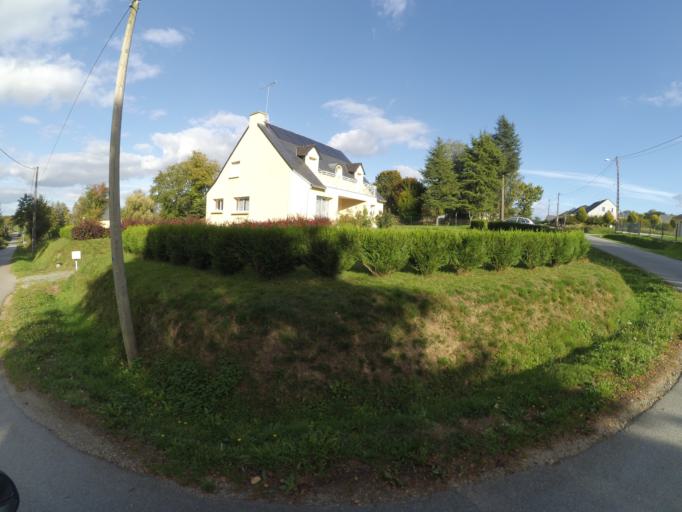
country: FR
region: Brittany
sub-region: Departement du Morbihan
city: Peillac
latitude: 47.7183
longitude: -2.2209
